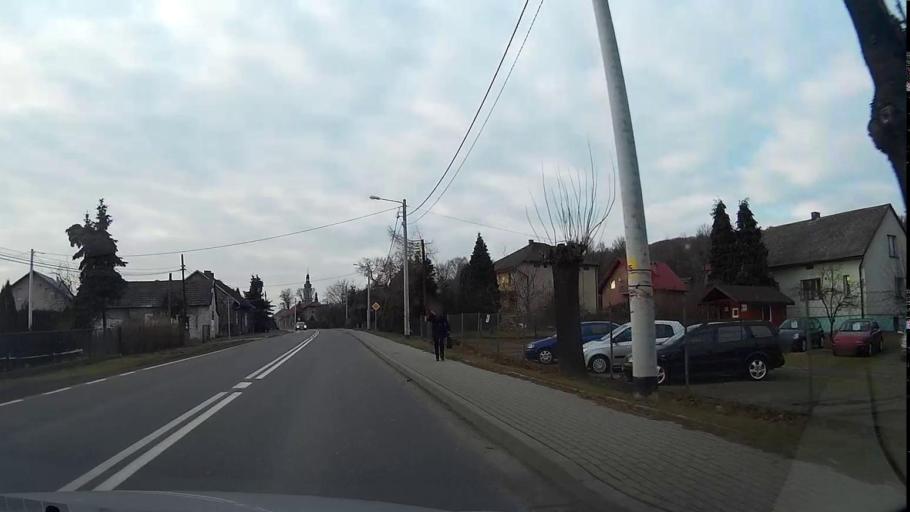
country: PL
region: Lesser Poland Voivodeship
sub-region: Powiat chrzanowski
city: Babice
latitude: 50.0702
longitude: 19.4582
